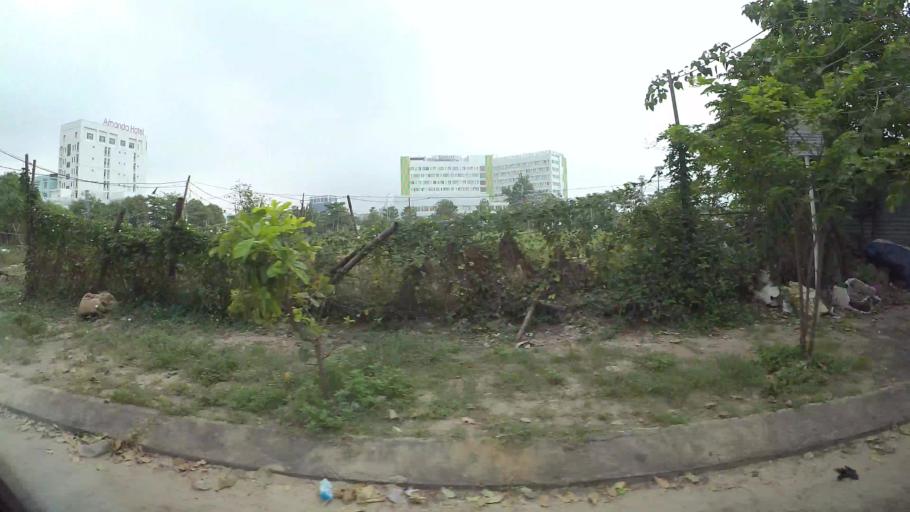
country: VN
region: Da Nang
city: Cam Le
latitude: 16.0408
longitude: 108.2115
